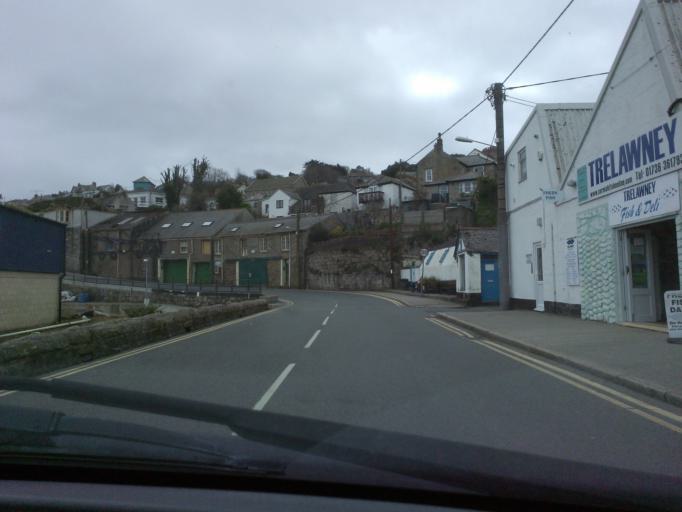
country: GB
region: England
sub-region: Cornwall
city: Penzance
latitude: 50.1037
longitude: -5.5496
